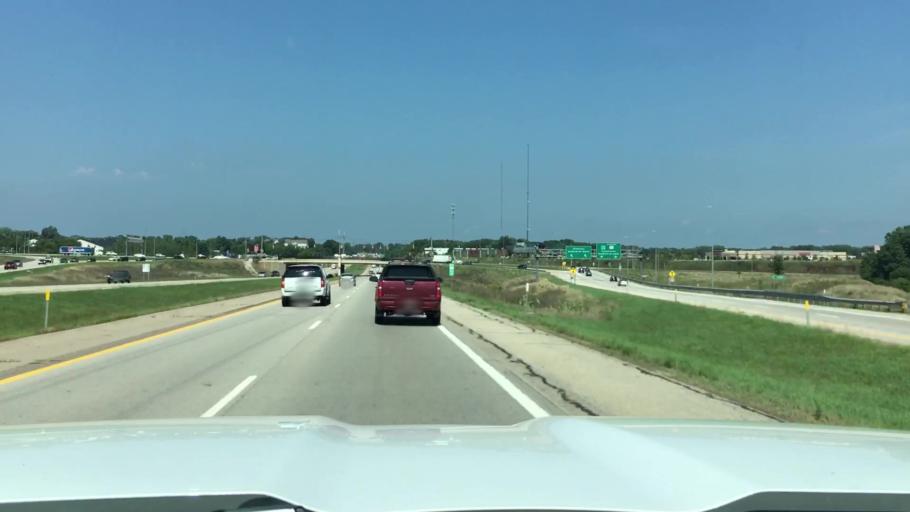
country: US
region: Michigan
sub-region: Kalamazoo County
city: Westwood
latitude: 42.2649
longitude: -85.6526
